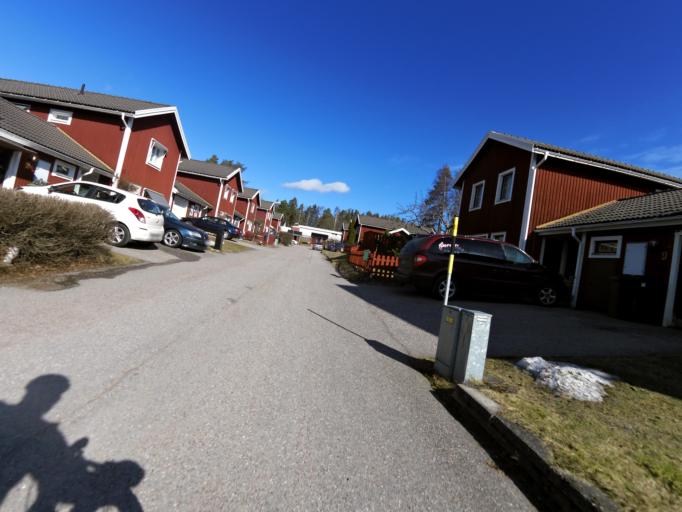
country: SE
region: Gaevleborg
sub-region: Hofors Kommun
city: Hofors
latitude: 60.5448
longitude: 16.2805
